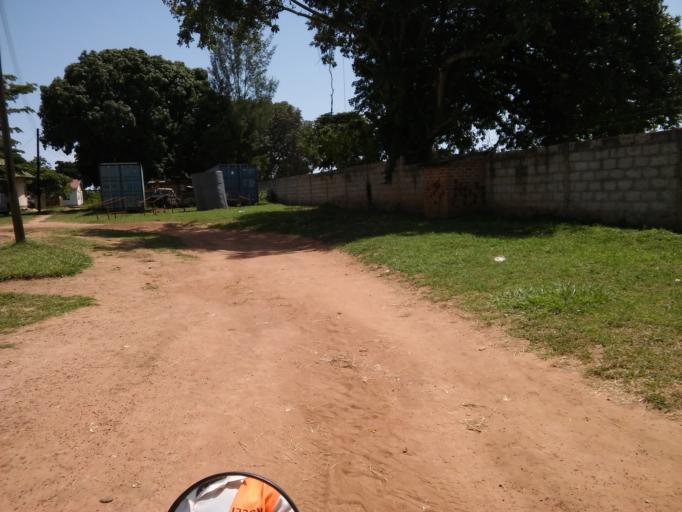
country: UG
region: Eastern Region
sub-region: Kumi District
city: Kumi
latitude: 1.4739
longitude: 33.8644
